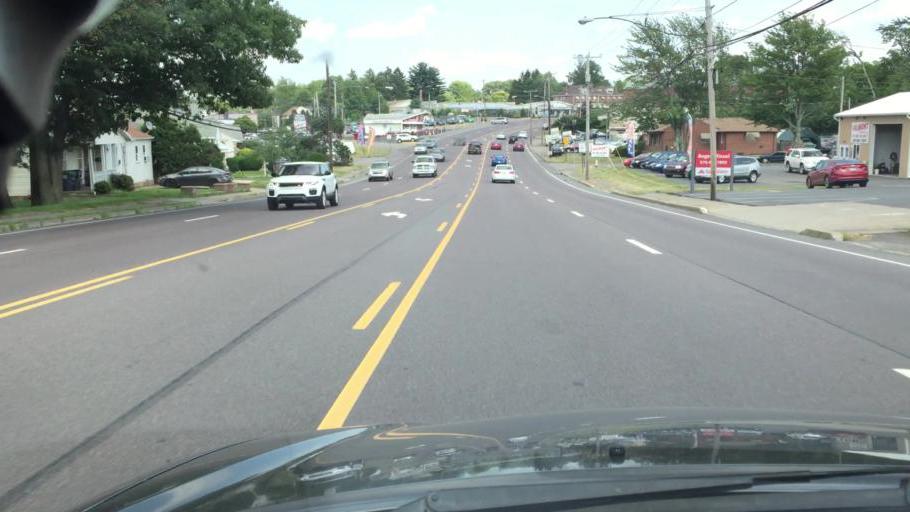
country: US
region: Pennsylvania
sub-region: Luzerne County
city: West Hazleton
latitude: 40.9665
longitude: -76.0016
